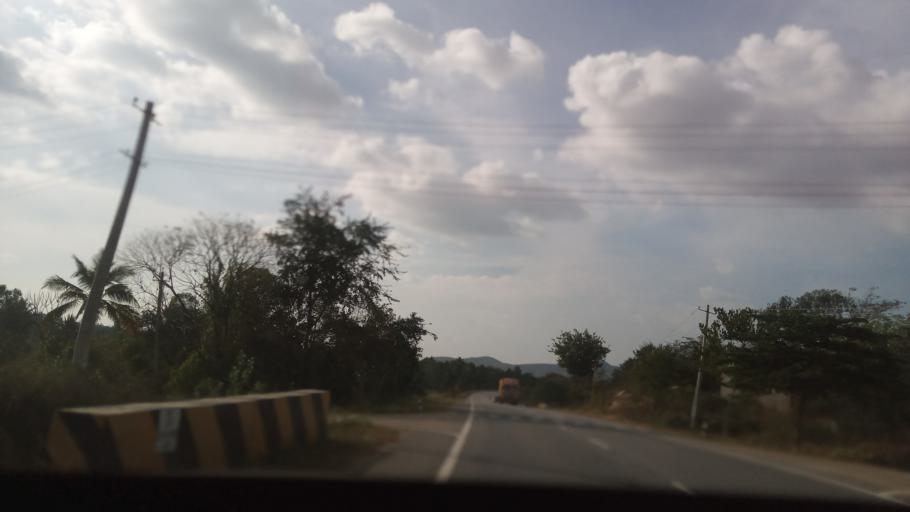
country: IN
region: Karnataka
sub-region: Tumkur
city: Kunigal
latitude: 12.8177
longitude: 77.0316
